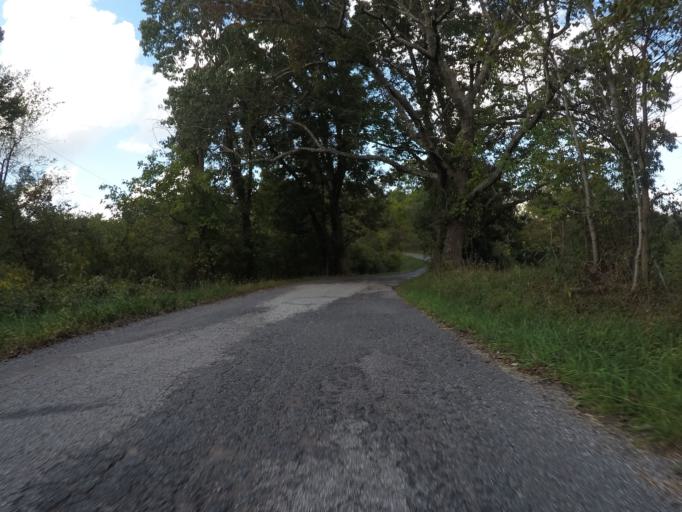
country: US
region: West Virginia
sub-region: Wayne County
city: Lavalette
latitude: 38.3619
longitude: -82.4668
